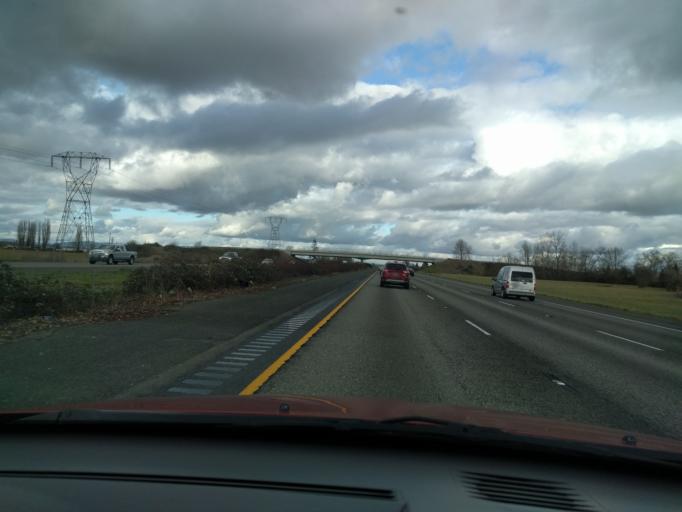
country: US
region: Oregon
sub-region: Marion County
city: Gervais
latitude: 45.1130
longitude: -122.9194
